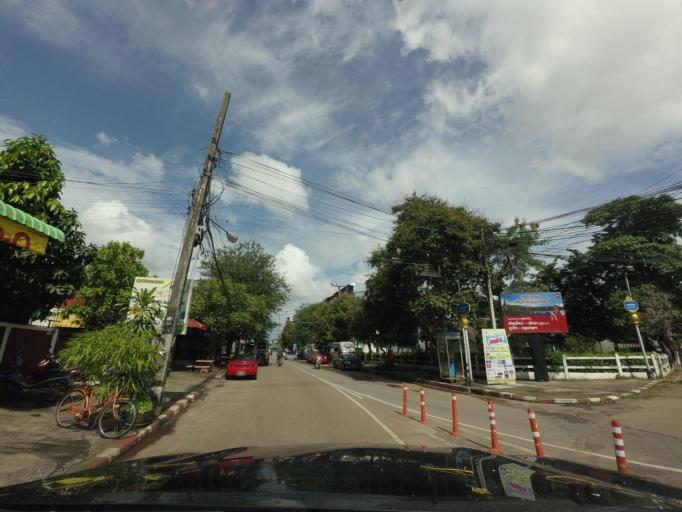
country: TH
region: Changwat Udon Thani
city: Udon Thani
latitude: 17.4068
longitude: 102.8040
